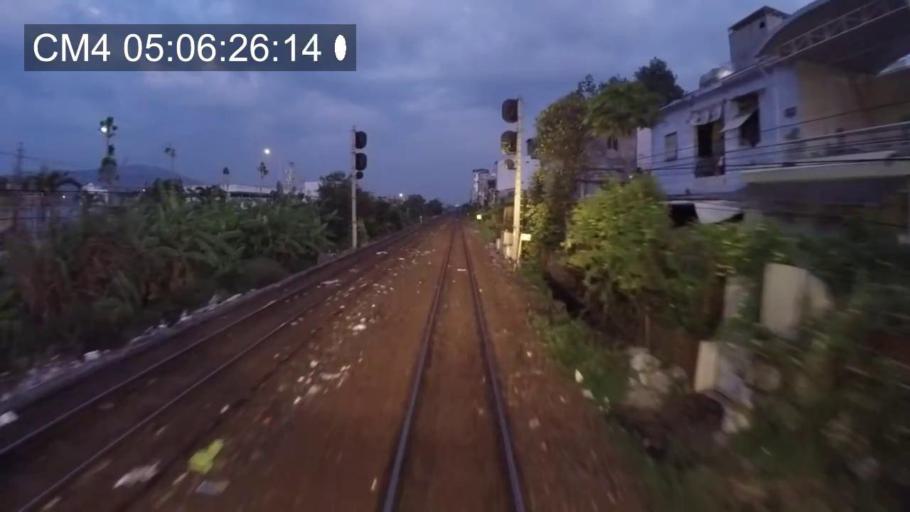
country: VN
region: Khanh Hoa
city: Nha Trang
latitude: 12.2779
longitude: 109.1801
